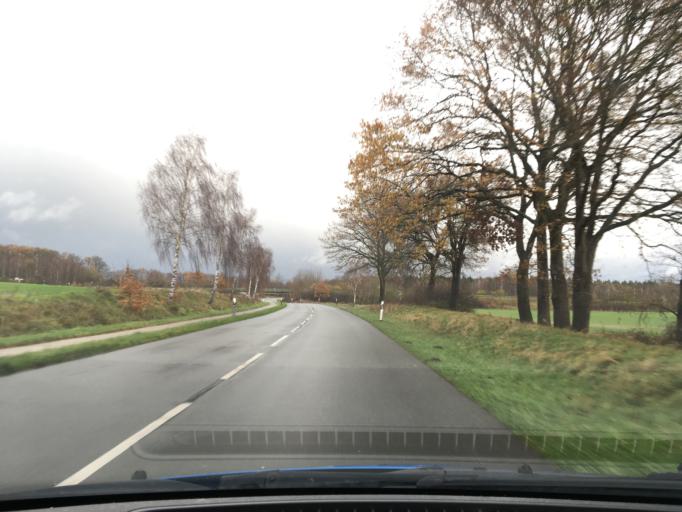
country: DE
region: Lower Saxony
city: Embsen
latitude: 53.1909
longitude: 10.3475
